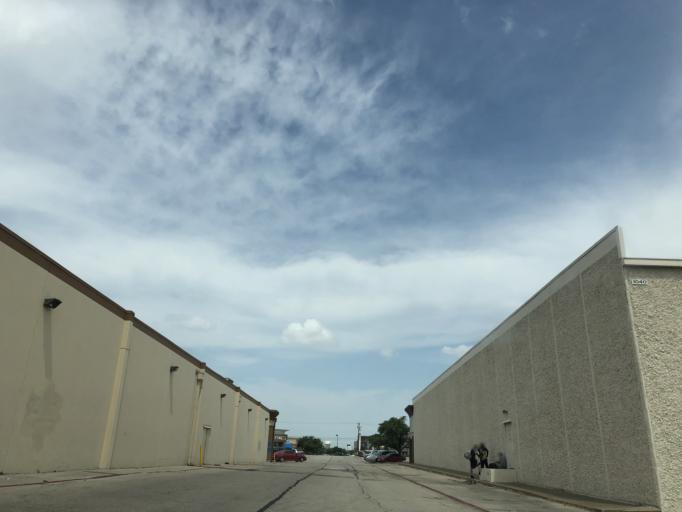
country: US
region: Texas
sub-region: Dallas County
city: Garland
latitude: 32.8563
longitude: -96.6447
